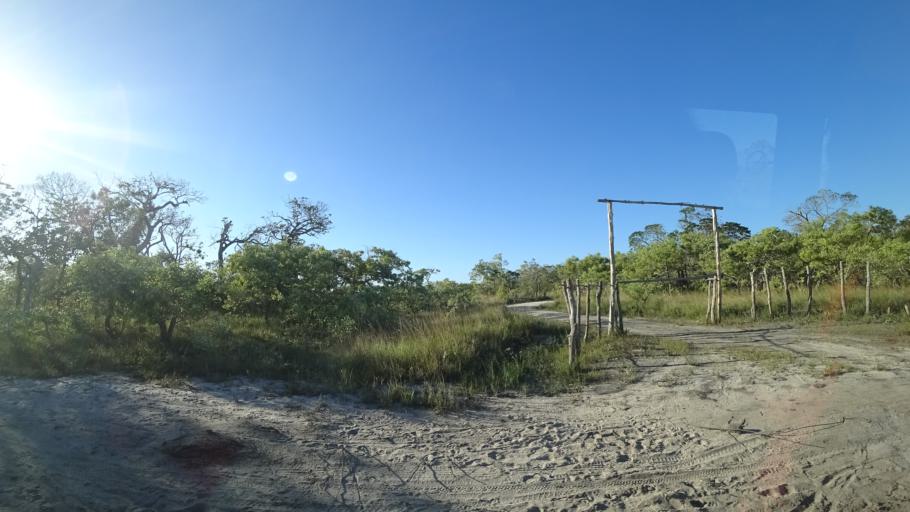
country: MZ
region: Sofala
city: Beira
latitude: -19.5764
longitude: 35.1965
